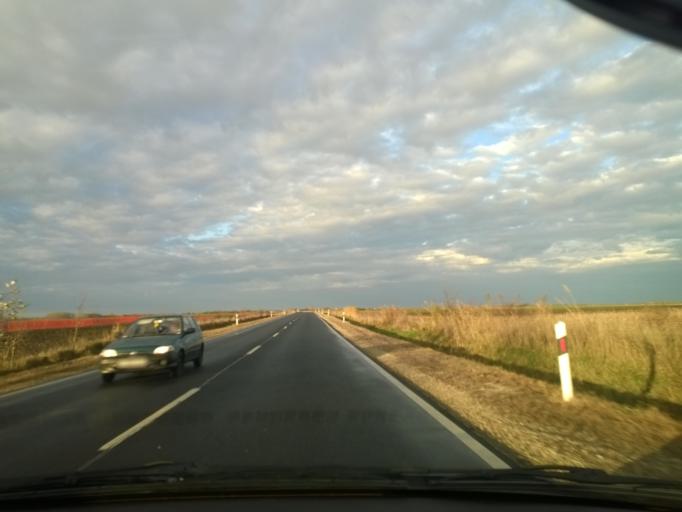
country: HU
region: Bacs-Kiskun
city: Dunapataj
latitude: 46.5901
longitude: 18.9780
